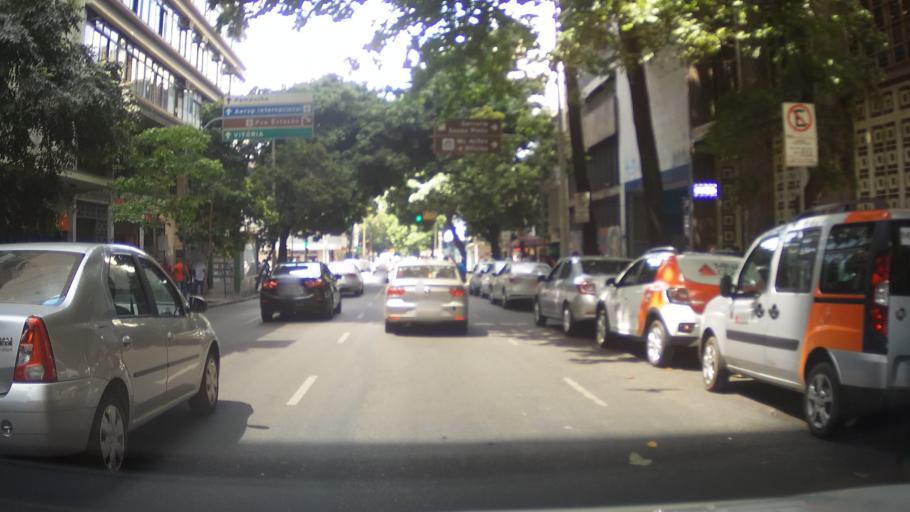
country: BR
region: Minas Gerais
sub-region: Belo Horizonte
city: Belo Horizonte
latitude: -19.9193
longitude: -43.9372
